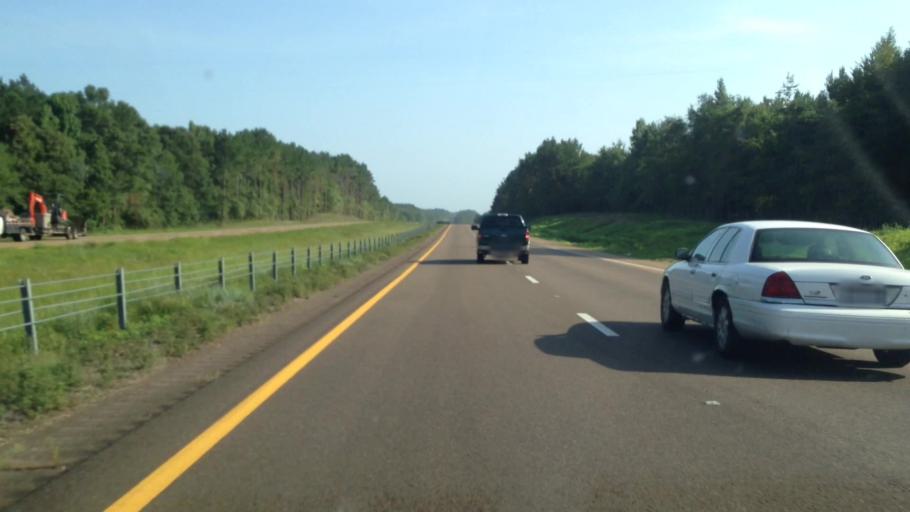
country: US
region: Mississippi
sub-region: Pike County
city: Summit
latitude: 31.4289
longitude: -90.4797
